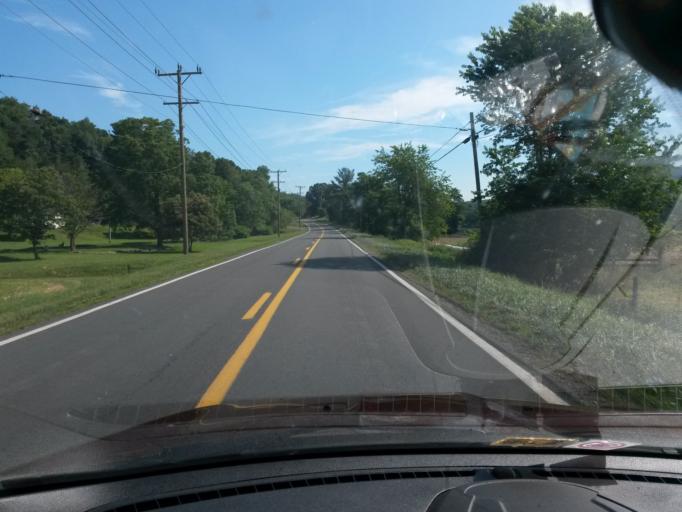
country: US
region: Virginia
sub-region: Shenandoah County
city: Basye
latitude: 38.8963
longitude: -78.8538
